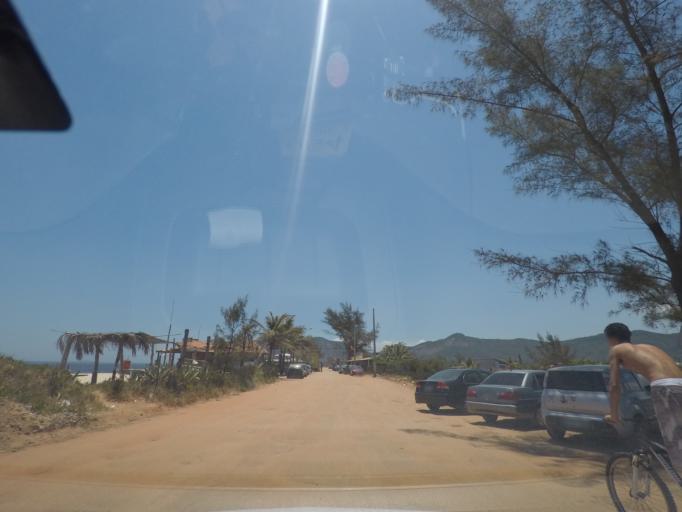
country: BR
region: Rio de Janeiro
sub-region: Niteroi
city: Niteroi
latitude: -22.9691
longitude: -42.9797
